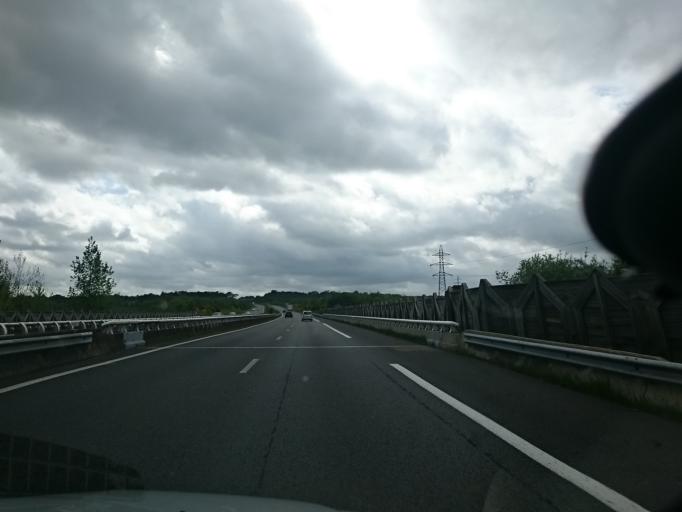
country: FR
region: Brittany
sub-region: Departement d'Ille-et-Vilaine
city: Gosne
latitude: 48.2390
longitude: -1.4687
